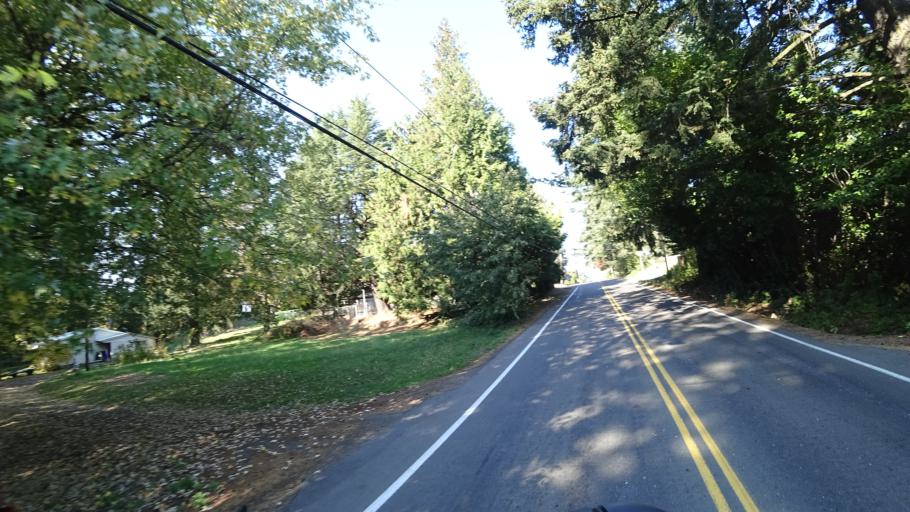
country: US
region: Oregon
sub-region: Multnomah County
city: Gresham
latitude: 45.4993
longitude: -122.4550
